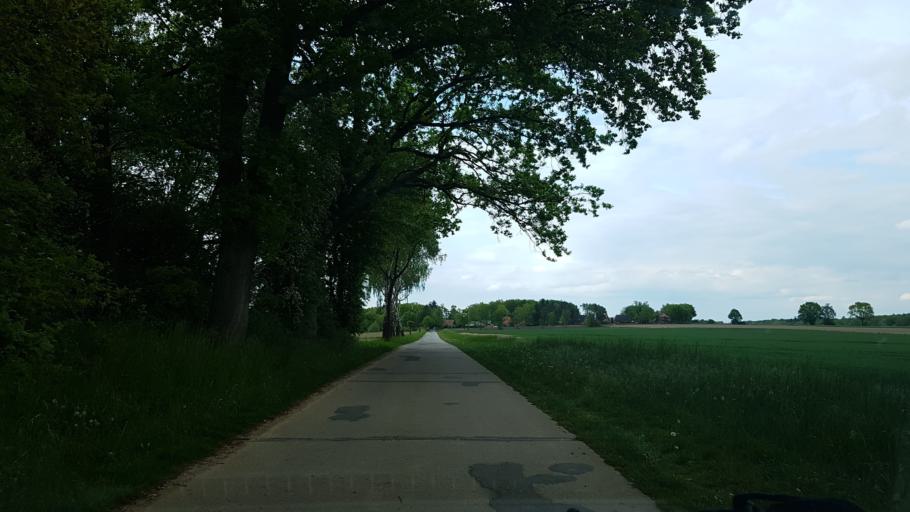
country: DE
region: Lower Saxony
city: Vastorf
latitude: 53.1810
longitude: 10.5515
